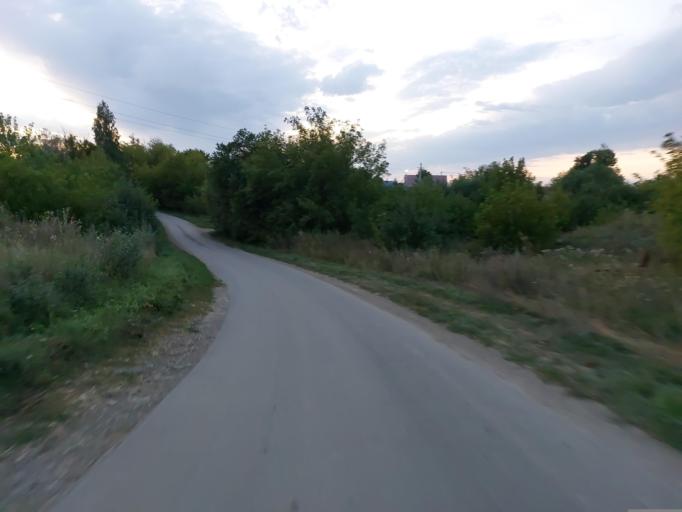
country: RU
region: Lipetsk
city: Dolgorukovo
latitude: 52.3790
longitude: 38.0476
